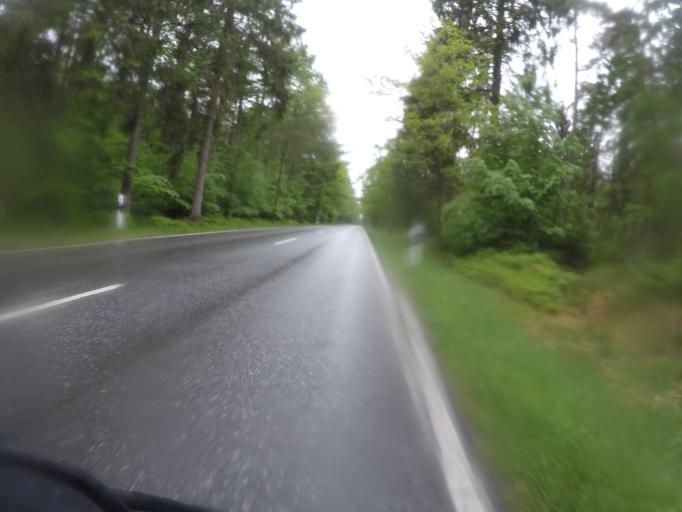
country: DE
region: Schleswig-Holstein
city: Heidmuhlen
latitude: 53.9430
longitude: 10.0870
